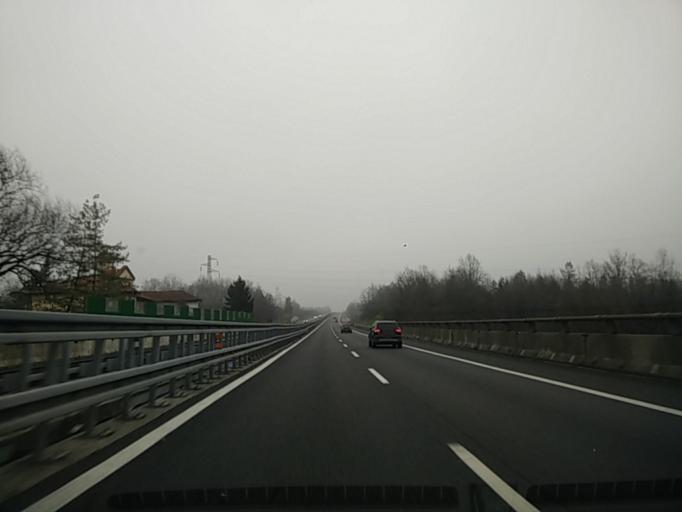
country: IT
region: Piedmont
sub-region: Provincia di Asti
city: Celle Enomondo
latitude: 44.9023
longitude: 8.1408
